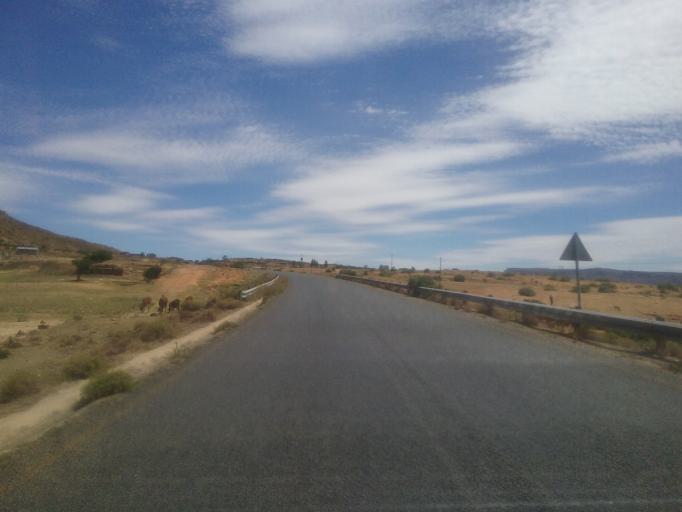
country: LS
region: Mohale's Hoek District
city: Mohale's Hoek
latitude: -30.0736
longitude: 27.4248
